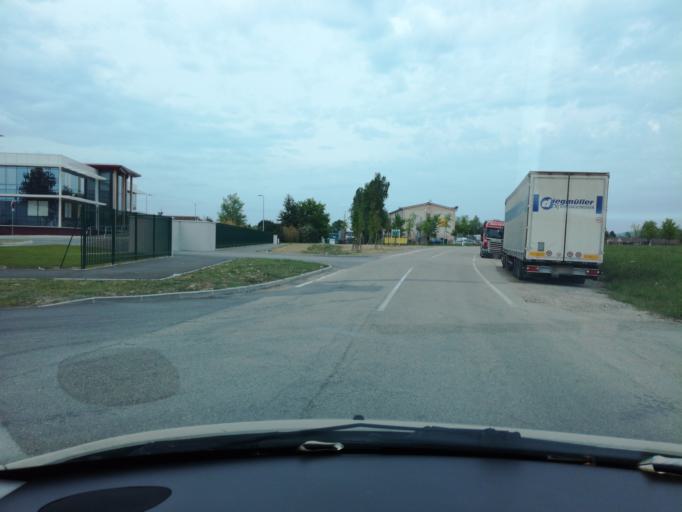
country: FR
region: Rhone-Alpes
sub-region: Departement de l'Ain
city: Certines
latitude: 46.1542
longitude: 5.2722
